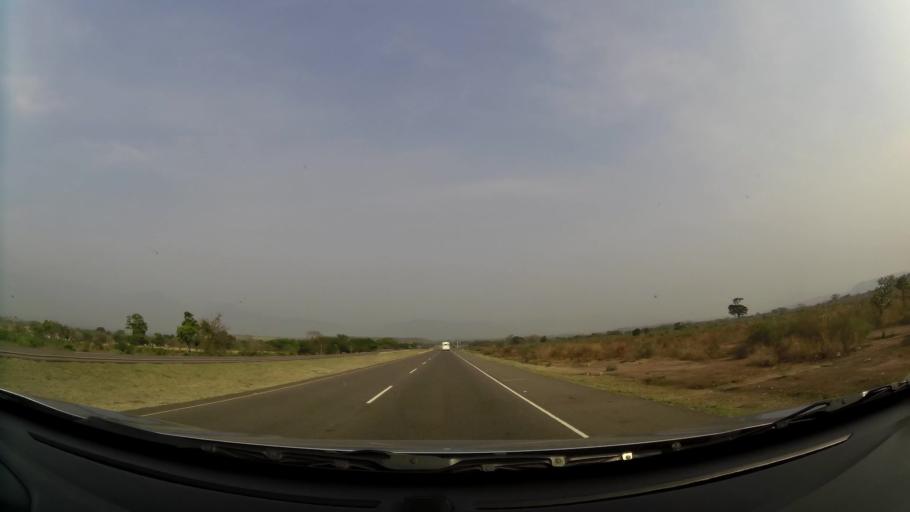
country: HN
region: Comayagua
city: Comayagua
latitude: 14.4301
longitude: -87.6434
